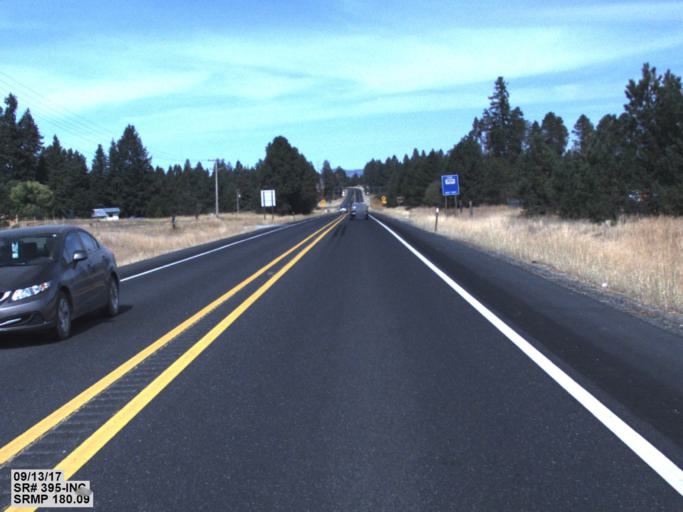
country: US
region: Washington
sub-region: Spokane County
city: Deer Park
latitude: 47.9494
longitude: -117.4839
